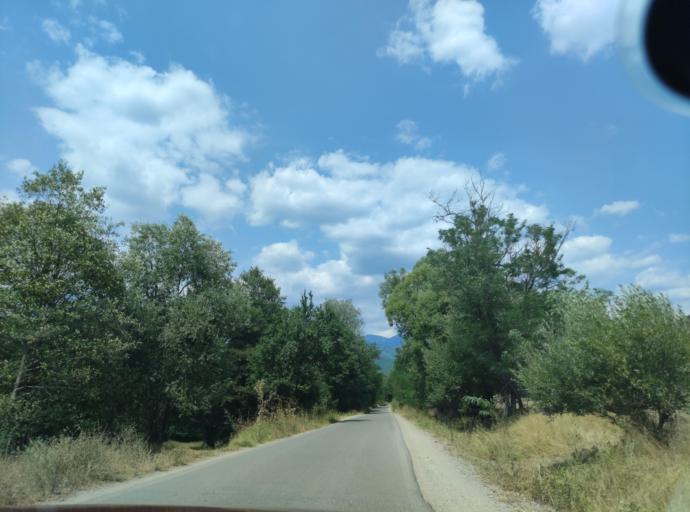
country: BG
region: Blagoevgrad
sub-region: Obshtina Belitsa
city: Belitsa
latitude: 41.9766
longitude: 23.5537
